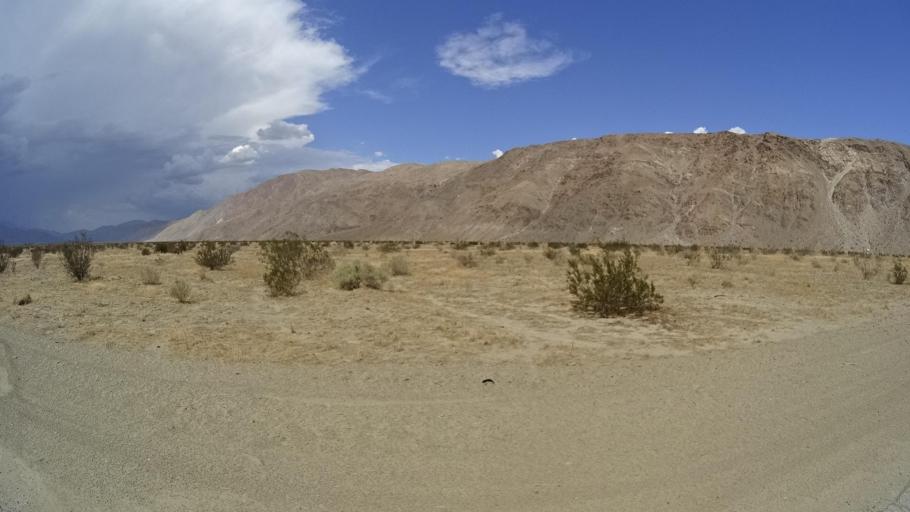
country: US
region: California
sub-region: San Diego County
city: Borrego Springs
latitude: 33.3009
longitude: -116.3198
